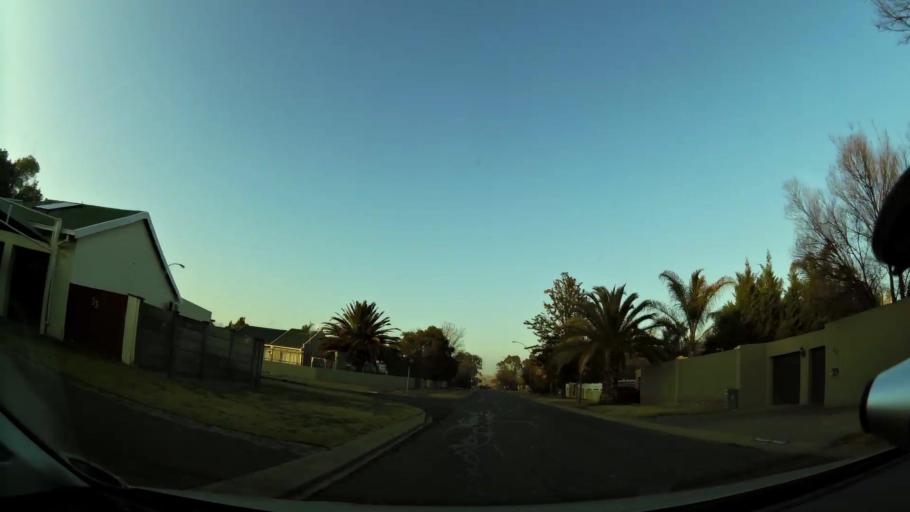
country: ZA
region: Orange Free State
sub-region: Mangaung Metropolitan Municipality
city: Bloemfontein
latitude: -29.1048
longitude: 26.1492
